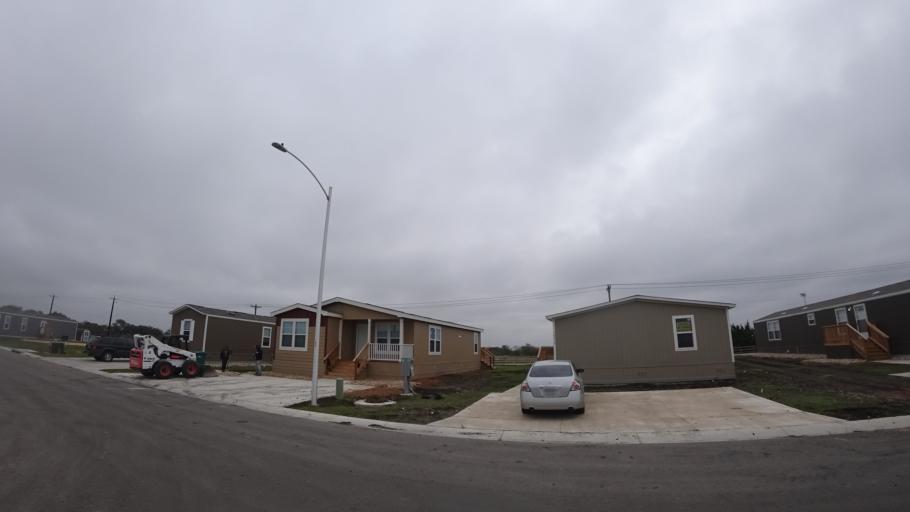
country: US
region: Texas
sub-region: Travis County
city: Pflugerville
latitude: 30.4069
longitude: -97.6043
